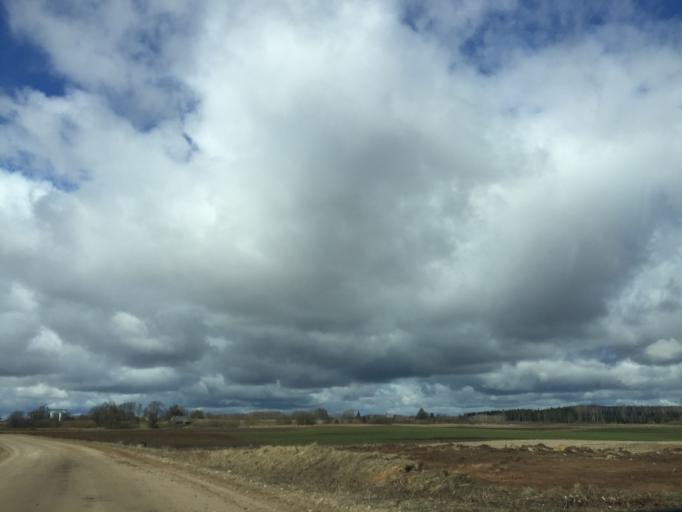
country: LV
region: Akniste
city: Akniste
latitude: 56.0996
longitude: 25.9751
